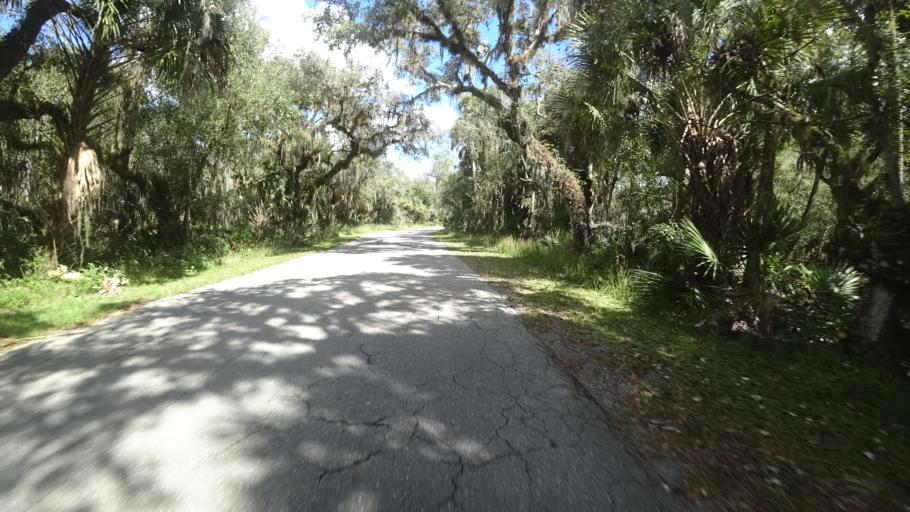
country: US
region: Florida
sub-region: Sarasota County
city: Lake Sarasota
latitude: 27.2780
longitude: -82.2650
